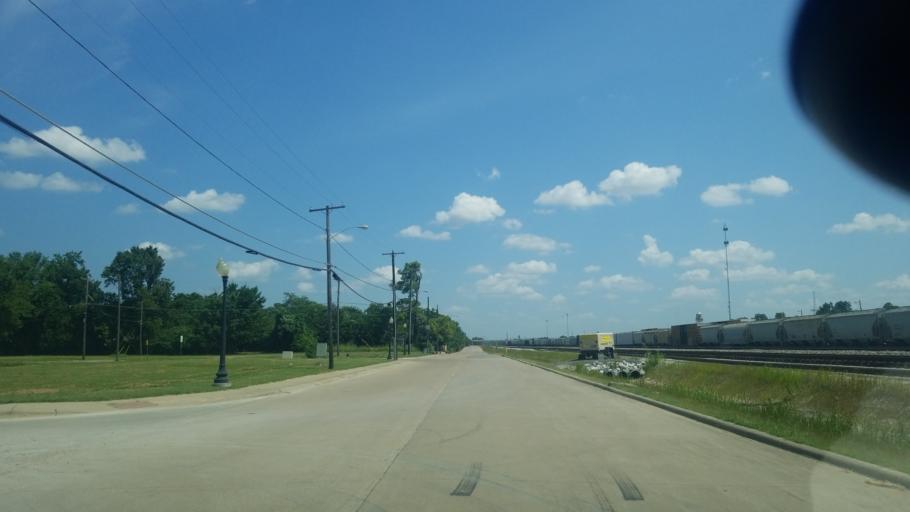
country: US
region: Texas
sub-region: Dallas County
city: Hutchins
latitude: 32.7149
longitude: -96.7499
